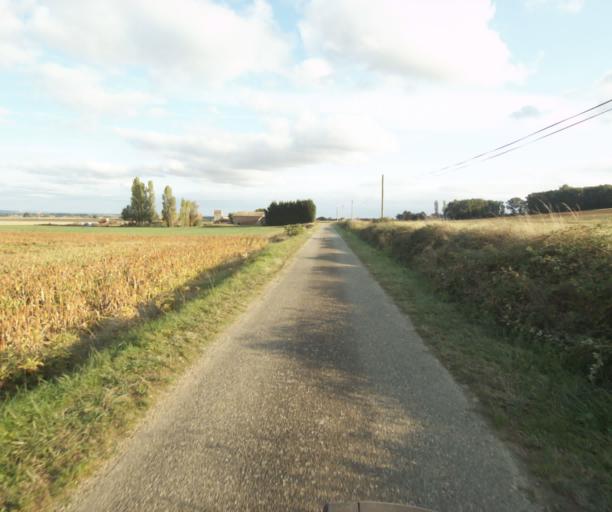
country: FR
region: Midi-Pyrenees
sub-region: Departement de la Haute-Garonne
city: Launac
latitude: 43.8158
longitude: 1.1368
